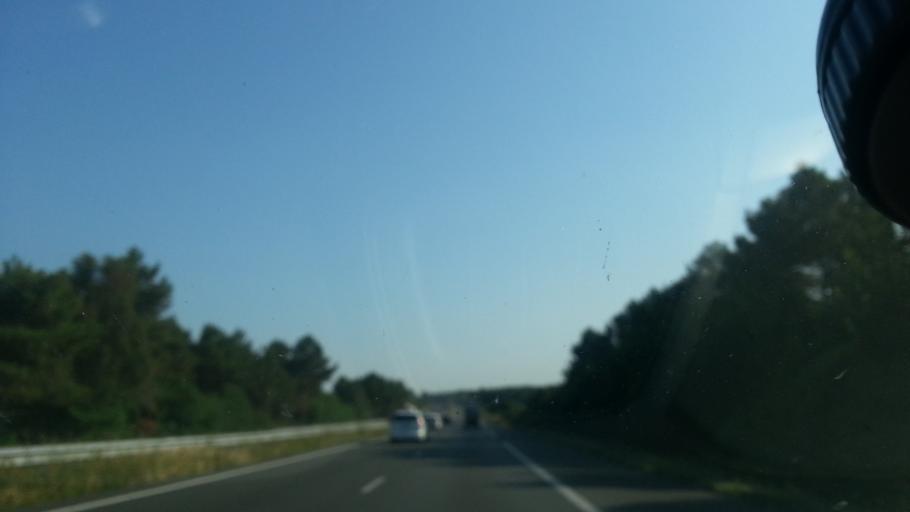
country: FR
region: Poitou-Charentes
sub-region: Departement de la Vienne
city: Dange-Saint-Romain
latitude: 46.9232
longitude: 0.5358
